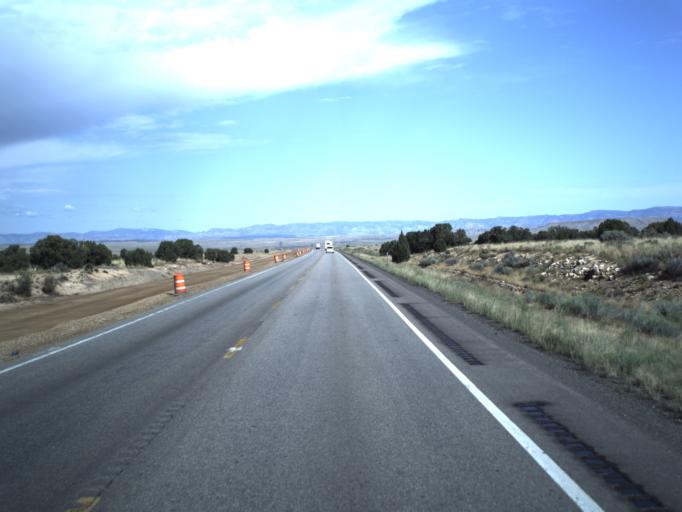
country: US
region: Utah
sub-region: Carbon County
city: East Carbon City
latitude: 39.4218
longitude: -110.4423
